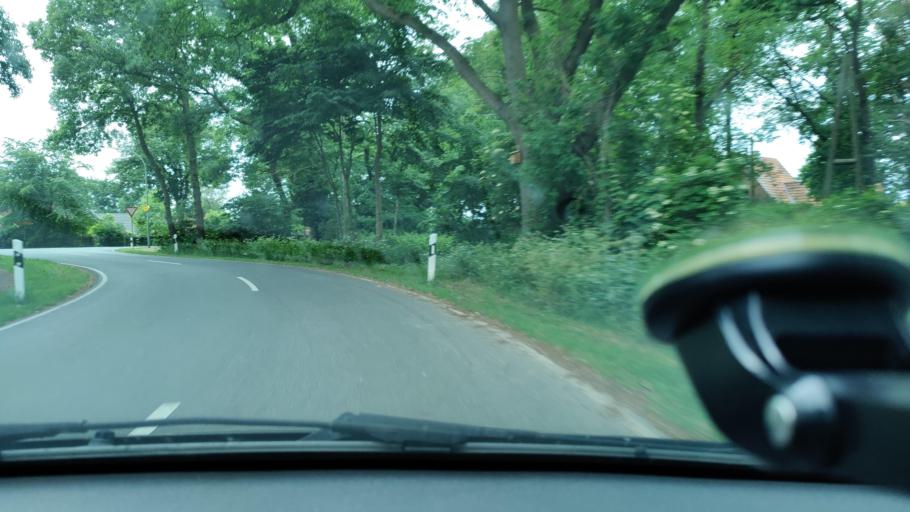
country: NL
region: Limburg
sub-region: Gemeente Gennep
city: Gennep
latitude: 51.6854
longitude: 6.0527
